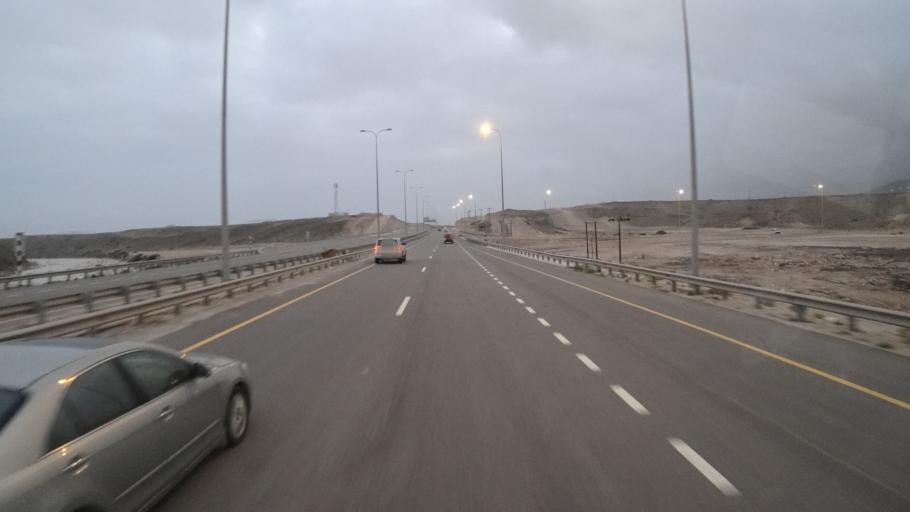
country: OM
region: Zufar
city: Salalah
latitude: 17.0498
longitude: 54.4687
